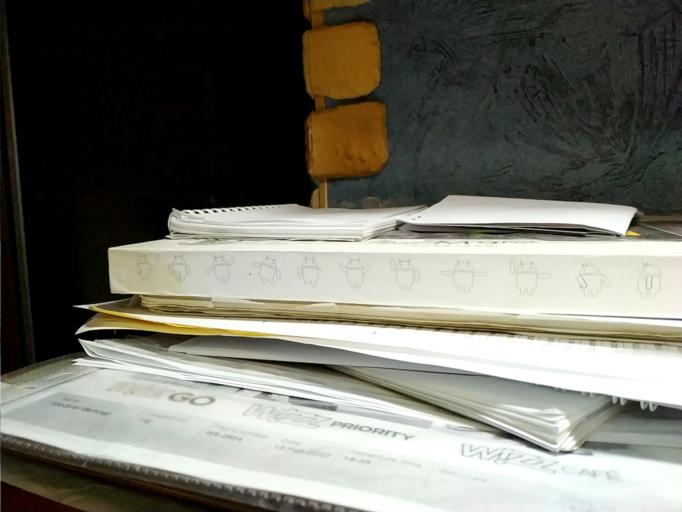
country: RU
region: Arkhangelskaya
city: Onega
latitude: 63.4853
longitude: 38.1544
